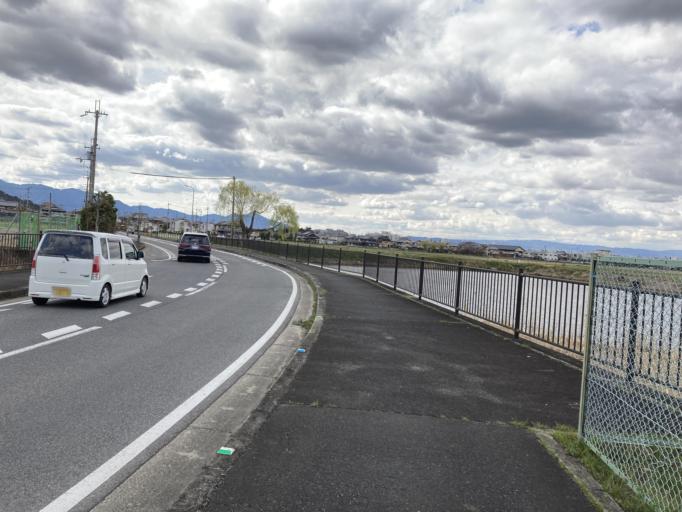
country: JP
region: Nara
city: Kashihara-shi
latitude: 34.4961
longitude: 135.8086
